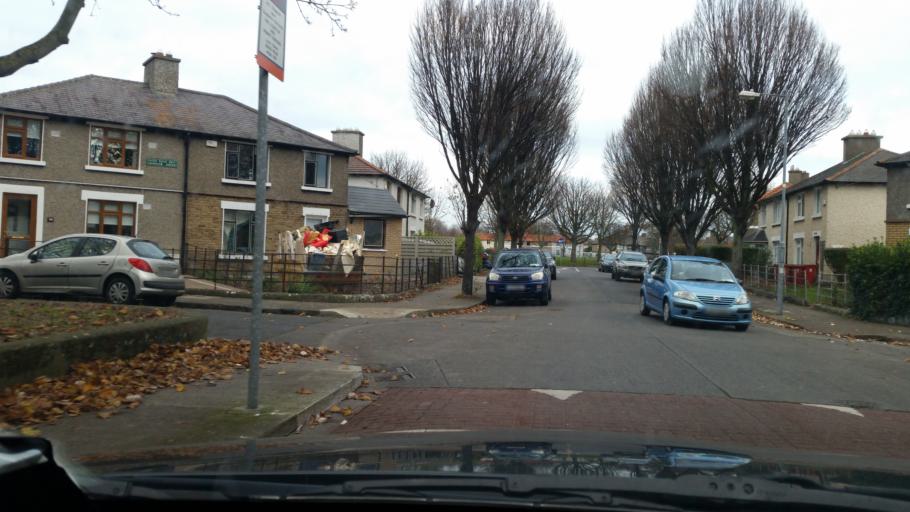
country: IE
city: Fairview
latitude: 53.3654
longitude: -6.2351
